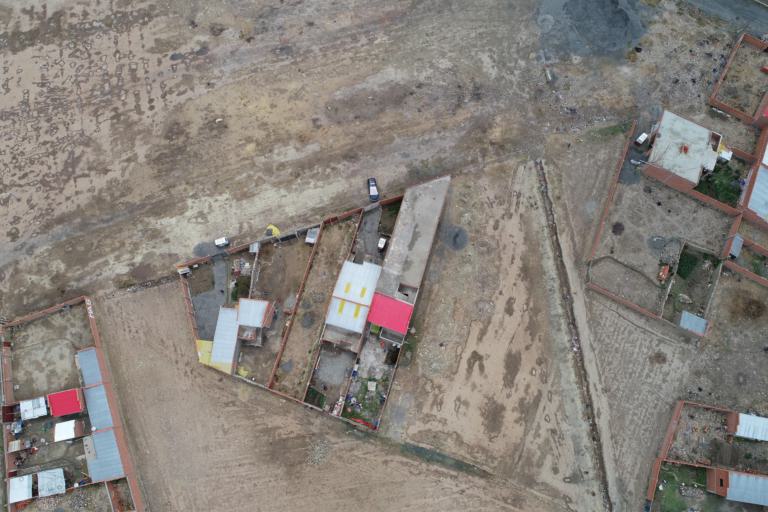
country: BO
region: La Paz
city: Achacachi
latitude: -16.0513
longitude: -68.6873
